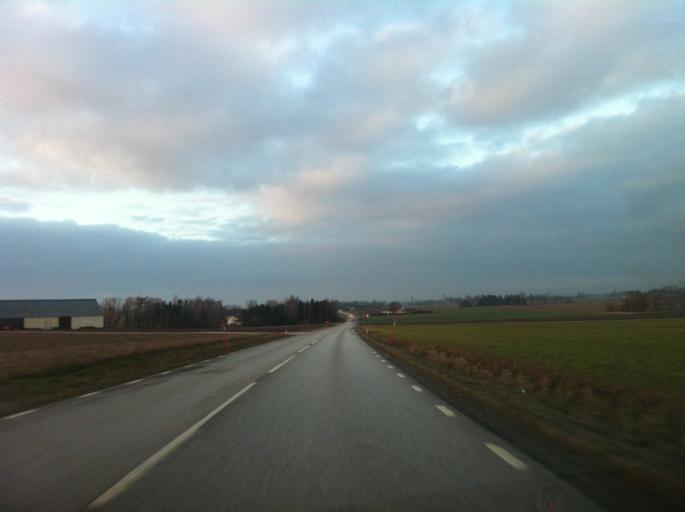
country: SE
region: Skane
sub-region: Kavlinge Kommun
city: Kaevlinge
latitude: 55.8019
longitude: 13.0938
